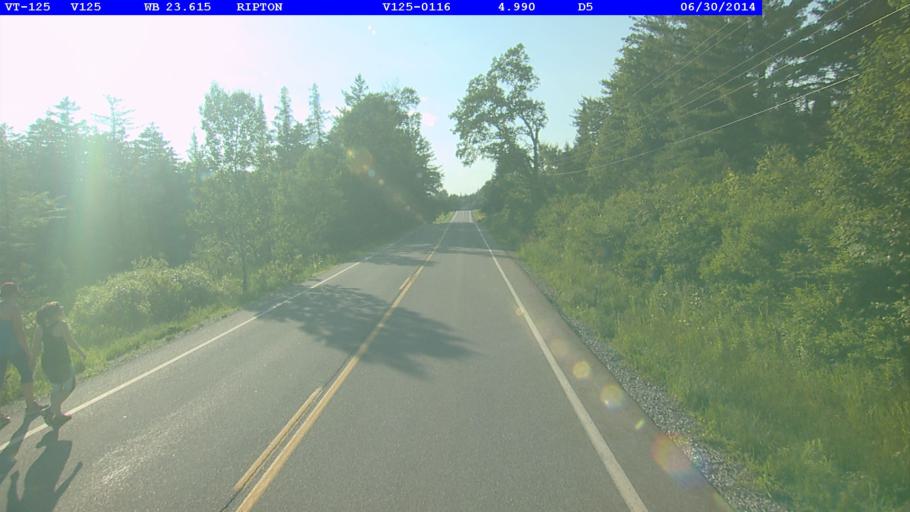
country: US
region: Vermont
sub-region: Rutland County
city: Brandon
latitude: 43.9474
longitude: -72.9810
